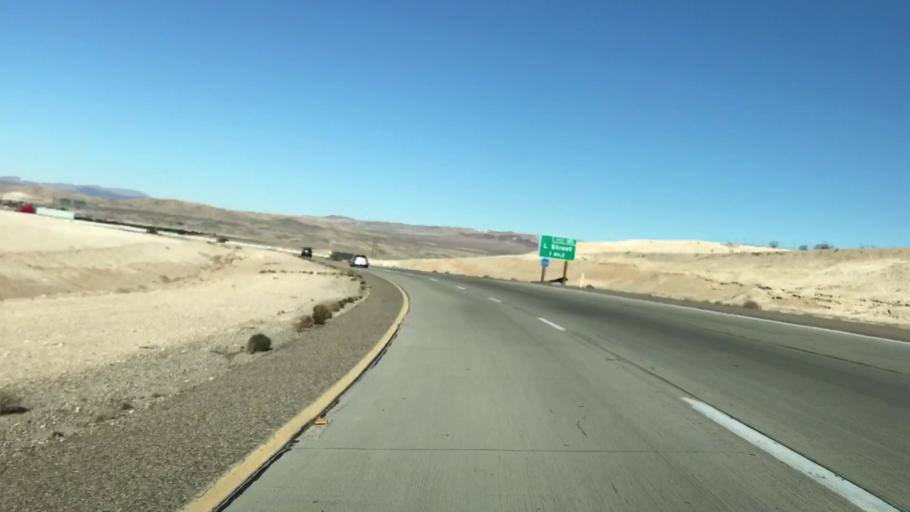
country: US
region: California
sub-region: San Bernardino County
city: Barstow Heights
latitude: 34.8722
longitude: -117.0703
